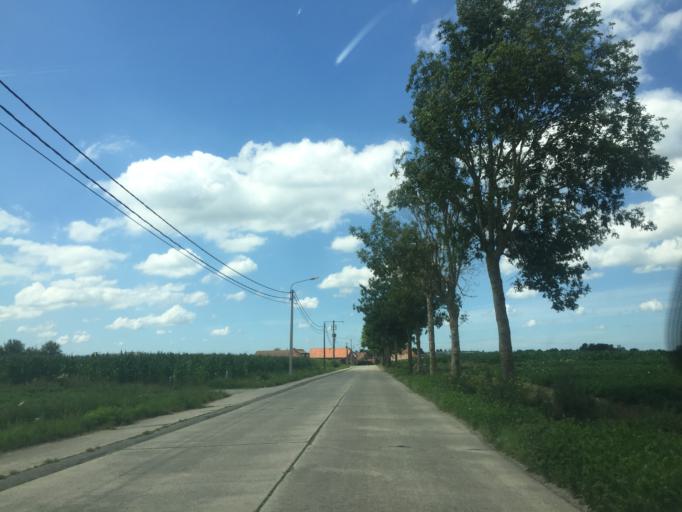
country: BE
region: Flanders
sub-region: Provincie West-Vlaanderen
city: Staden
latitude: 51.0041
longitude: 3.0133
